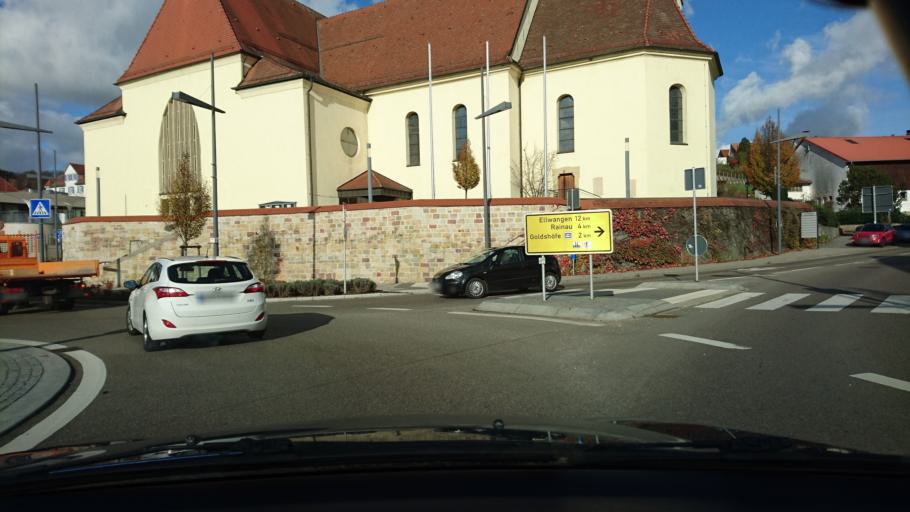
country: DE
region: Baden-Wuerttemberg
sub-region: Regierungsbezirk Stuttgart
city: Huttlingen
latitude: 48.8924
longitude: 10.1007
